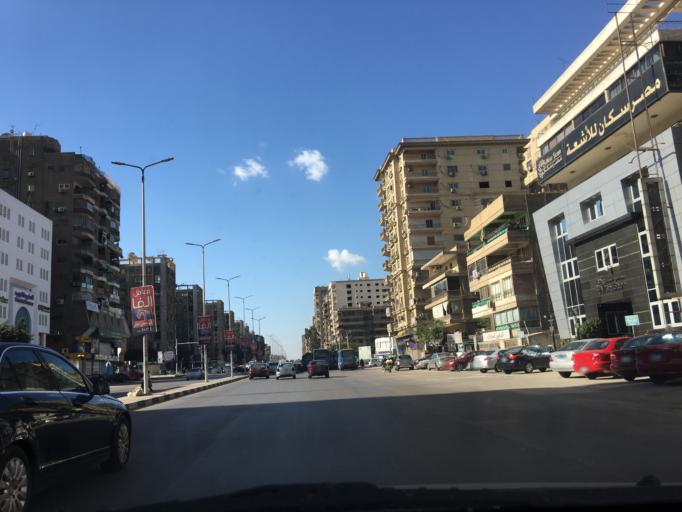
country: EG
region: Muhafazat al Qahirah
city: Cairo
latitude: 30.0540
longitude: 31.3399
